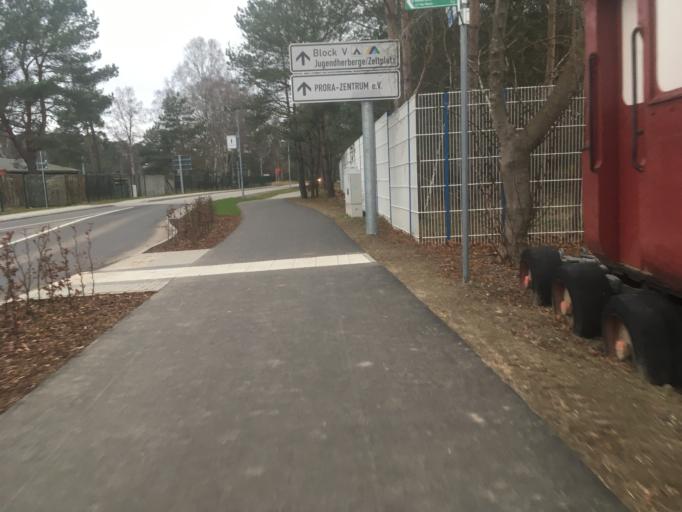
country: DE
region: Mecklenburg-Vorpommern
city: Ostseebad Binz
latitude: 54.4428
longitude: 13.5663
